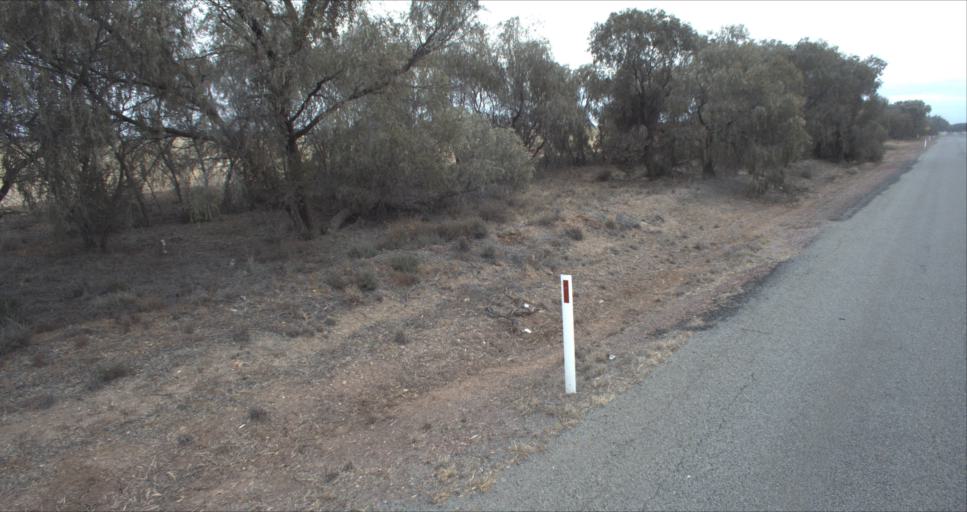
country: AU
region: New South Wales
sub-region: Leeton
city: Leeton
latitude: -34.4806
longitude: 146.3997
